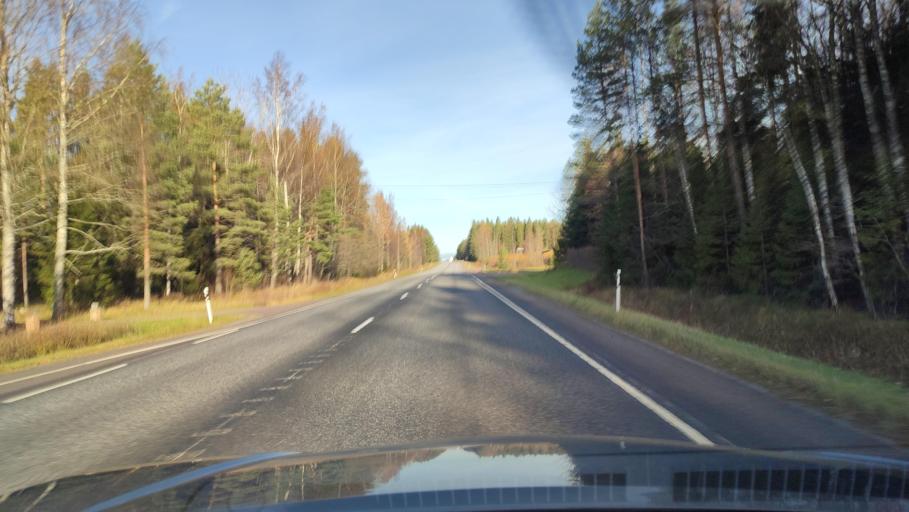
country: FI
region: Ostrobothnia
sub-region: Vaasa
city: Malax
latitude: 62.8135
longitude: 21.6839
